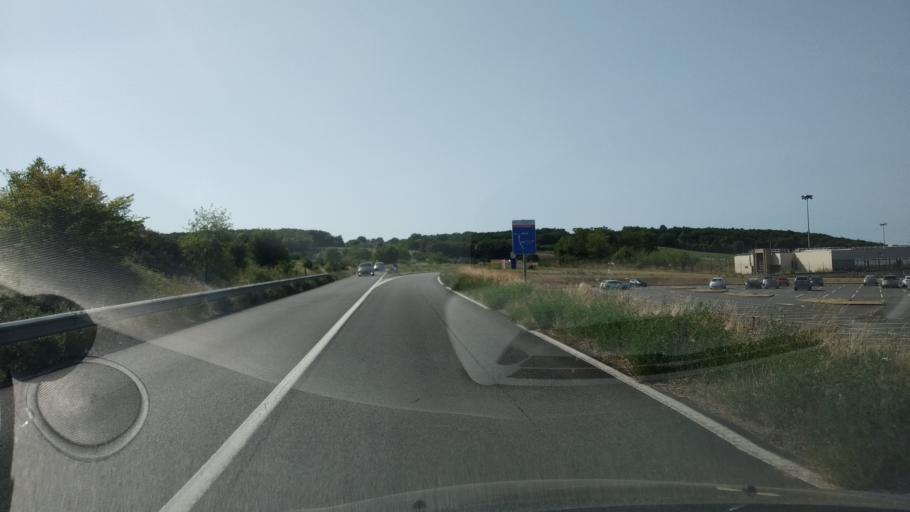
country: FR
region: Poitou-Charentes
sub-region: Departement de la Vienne
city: Lussac-les-Chateaux
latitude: 46.4480
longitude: 0.6523
